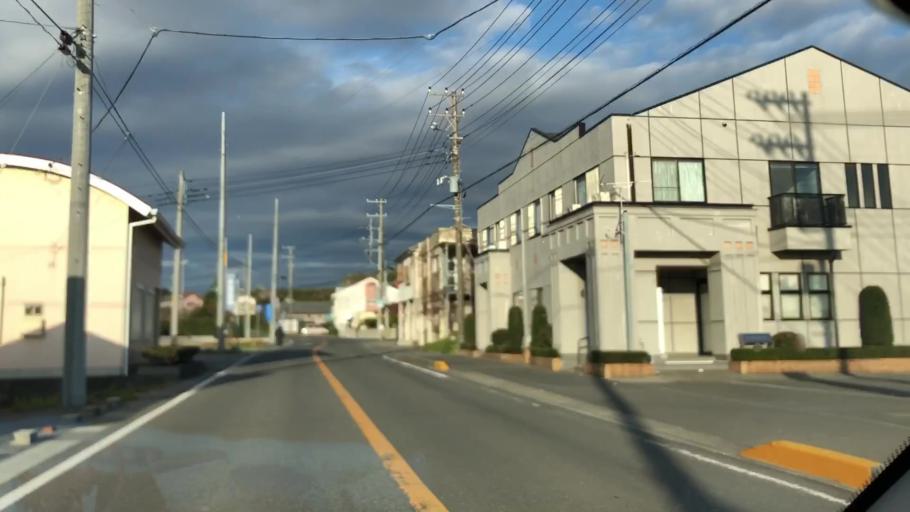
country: JP
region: Chiba
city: Tateyama
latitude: 34.9752
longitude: 139.9582
